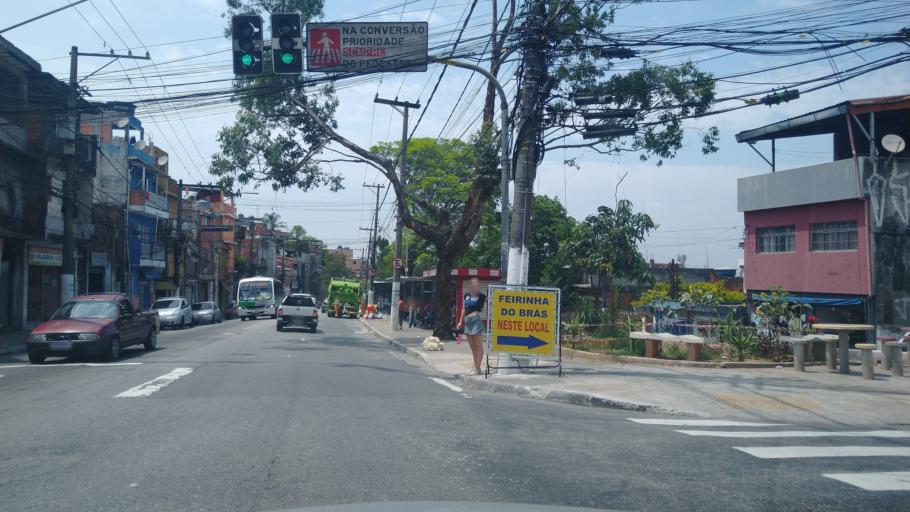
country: BR
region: Sao Paulo
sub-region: Sao Paulo
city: Sao Paulo
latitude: -23.4595
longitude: -46.6860
